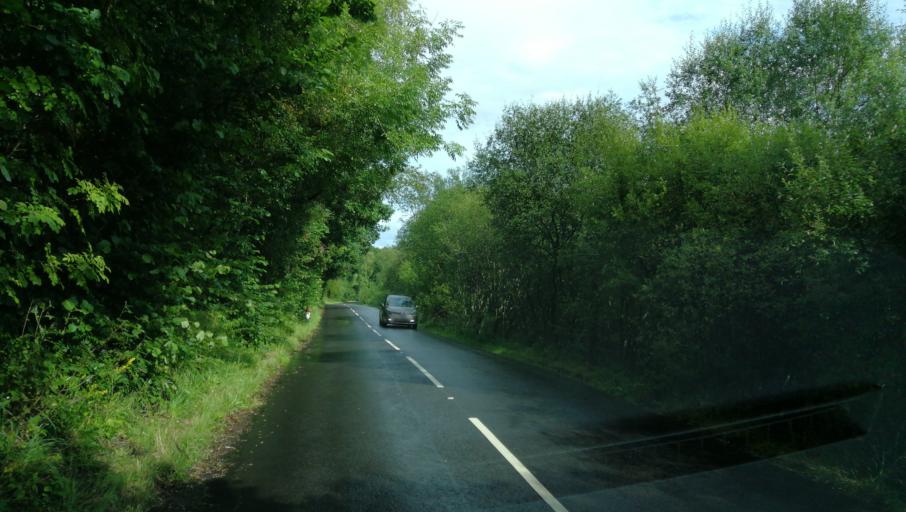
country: GB
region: Scotland
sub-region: Stirling
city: Callander
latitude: 56.2296
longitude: -4.3535
